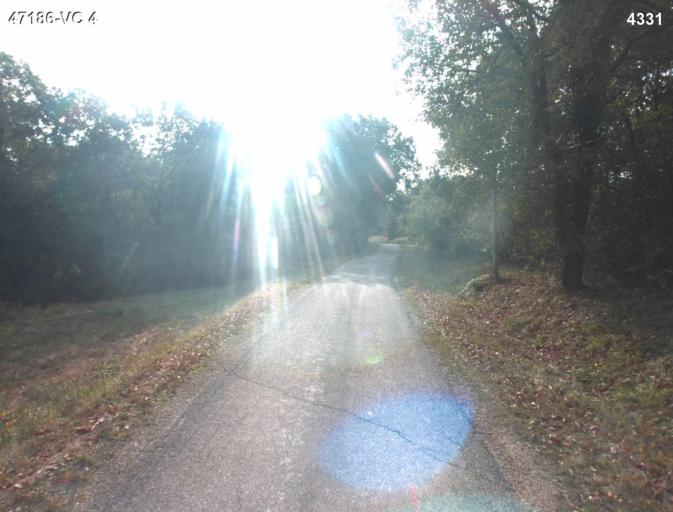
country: FR
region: Aquitaine
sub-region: Departement du Lot-et-Garonne
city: Sainte-Colombe-en-Bruilhois
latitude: 44.1948
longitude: 0.4508
